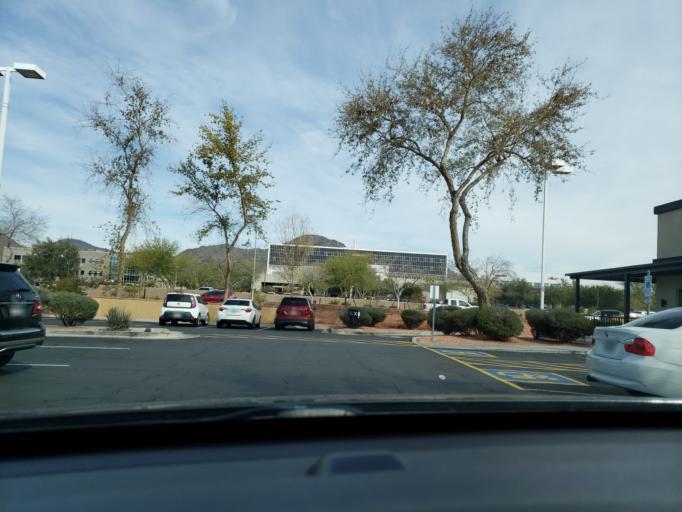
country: US
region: Arizona
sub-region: Maricopa County
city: Glendale
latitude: 33.5673
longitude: -112.0711
